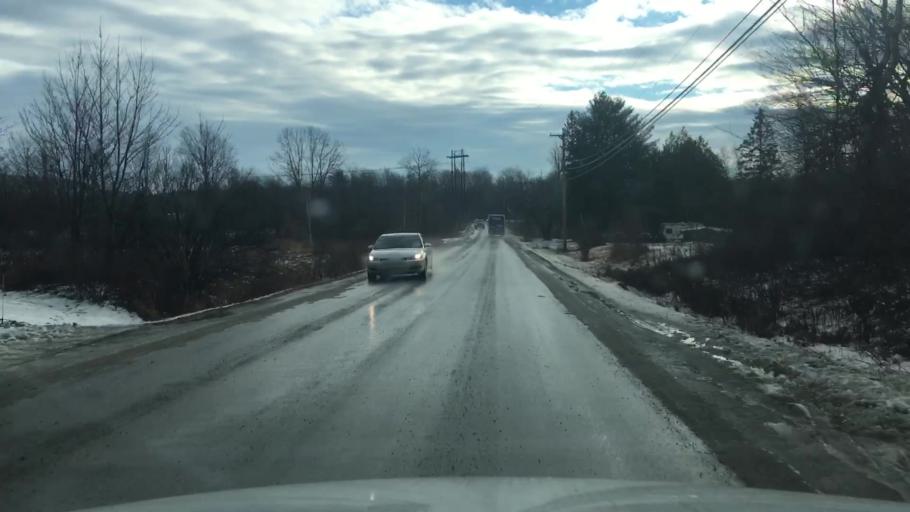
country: US
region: Maine
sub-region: Penobscot County
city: Brewer
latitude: 44.7309
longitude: -68.7587
